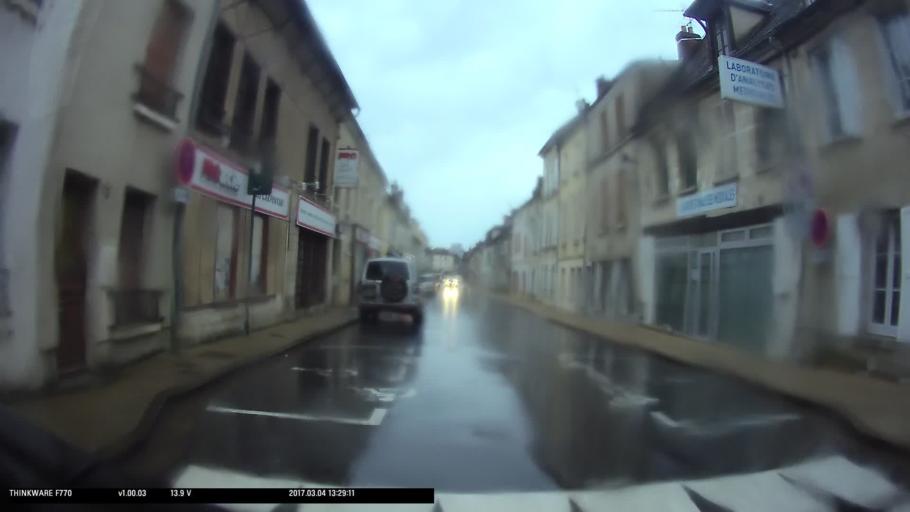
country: FR
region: Ile-de-France
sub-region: Departement du Val-d'Oise
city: Marines
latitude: 49.1440
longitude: 1.9796
